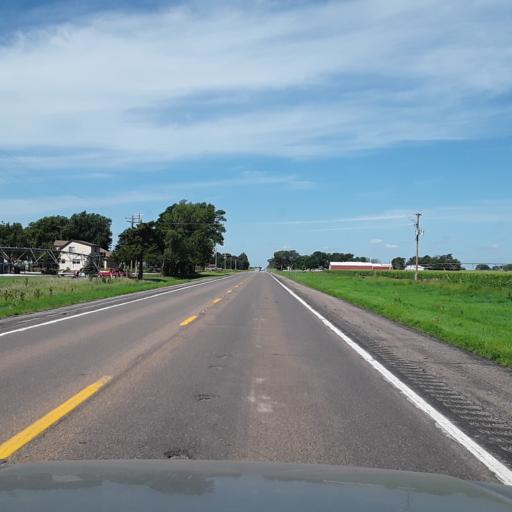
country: US
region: Nebraska
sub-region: Seward County
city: Seward
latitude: 40.9017
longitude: -97.1688
